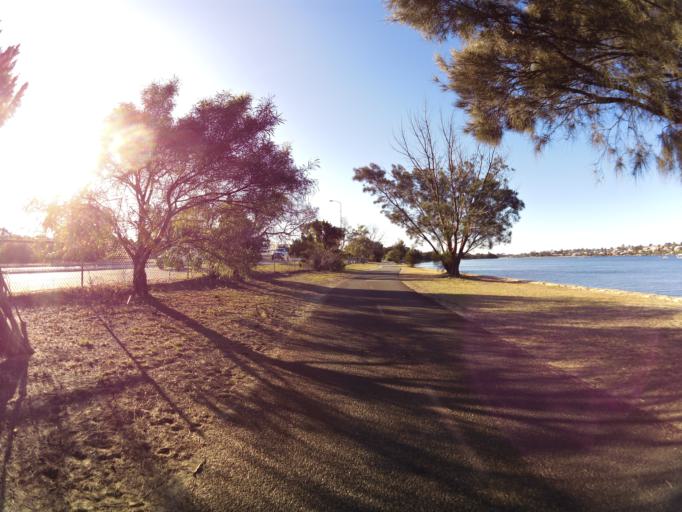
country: AU
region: Western Australia
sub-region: South Perth
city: Manning
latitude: -32.0120
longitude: 115.8563
